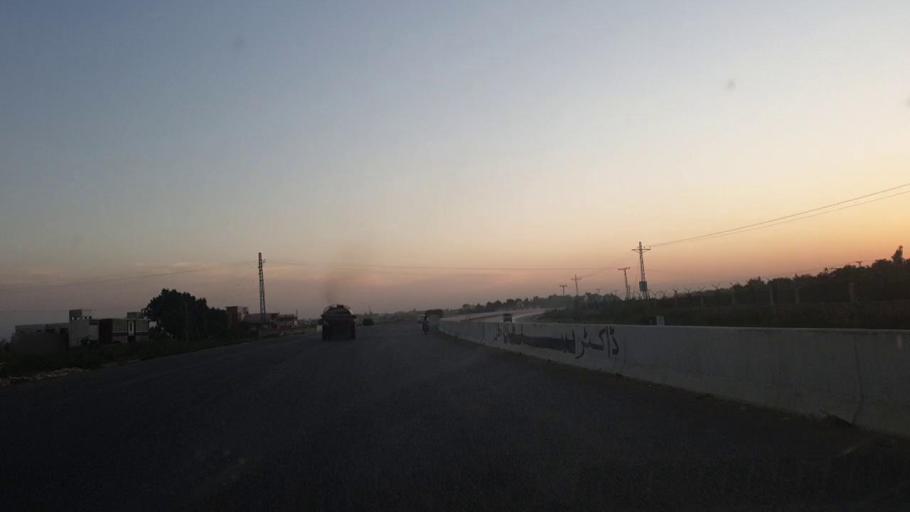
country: PK
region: Sindh
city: Jamshoro
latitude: 25.4214
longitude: 68.2803
